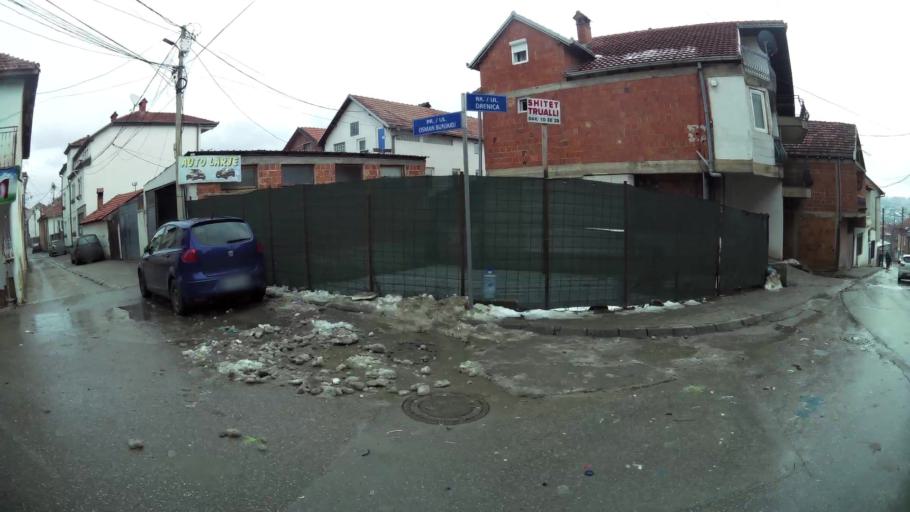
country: XK
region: Pristina
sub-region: Komuna e Prishtines
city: Pristina
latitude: 42.6756
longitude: 21.1659
